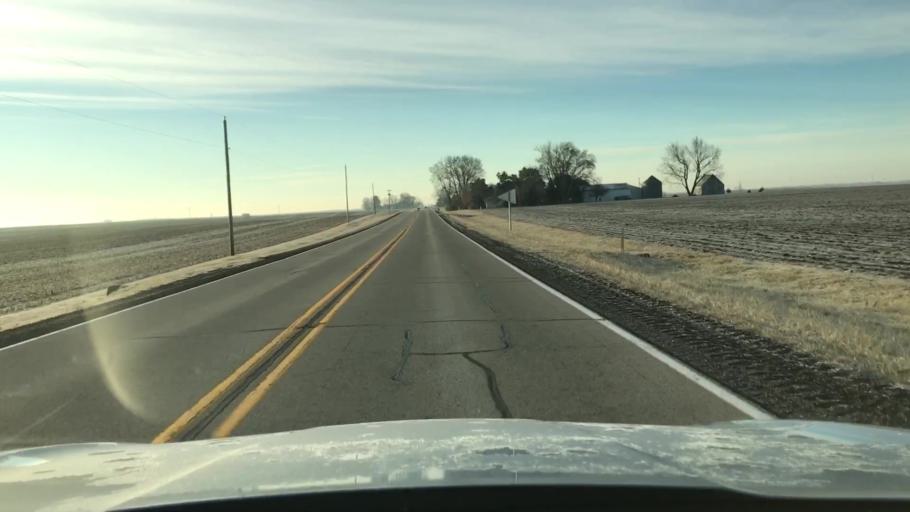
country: US
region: Illinois
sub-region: McLean County
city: Hudson
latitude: 40.6125
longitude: -88.9454
